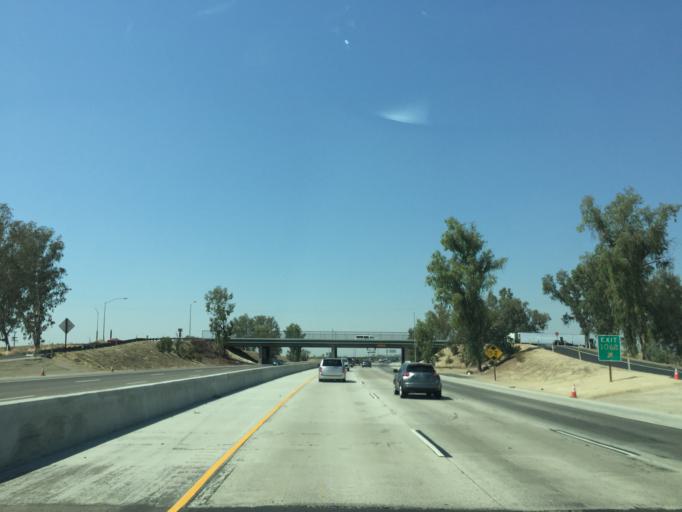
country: US
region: California
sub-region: Tulare County
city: London
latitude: 36.4510
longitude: -119.4896
